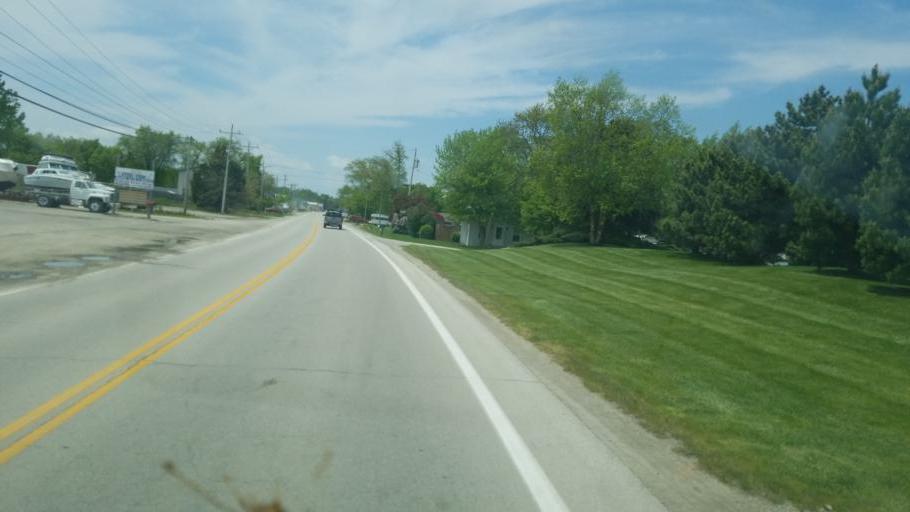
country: US
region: Ohio
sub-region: Ottawa County
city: Port Clinton
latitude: 41.5215
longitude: -82.9625
